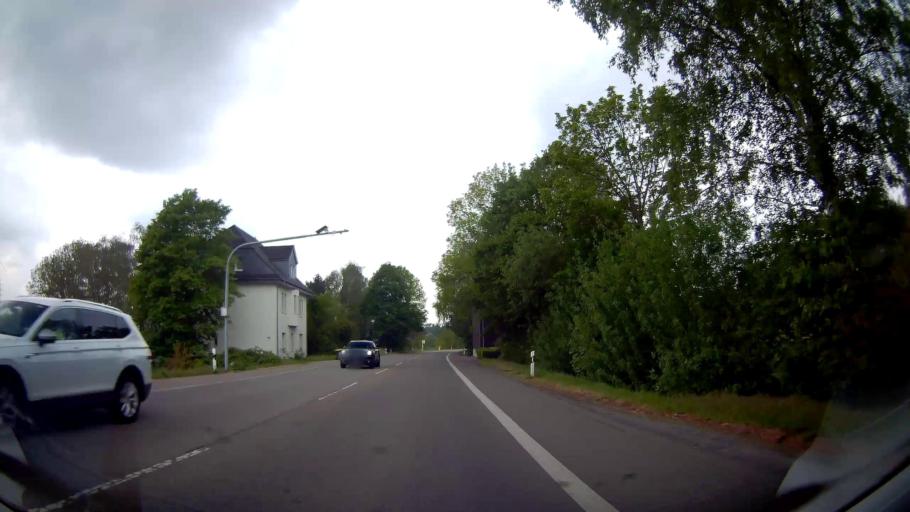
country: DE
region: North Rhine-Westphalia
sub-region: Regierungsbezirk Munster
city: Gladbeck
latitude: 51.5817
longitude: 6.9512
